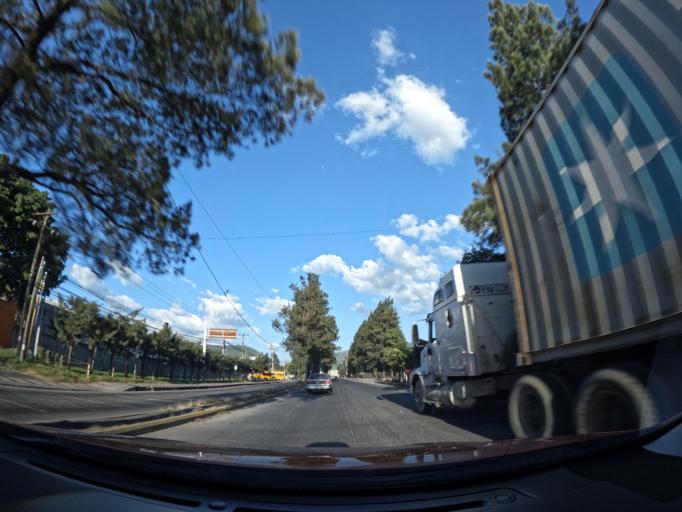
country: GT
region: Escuintla
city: Palin
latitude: 14.4074
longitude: -90.6880
